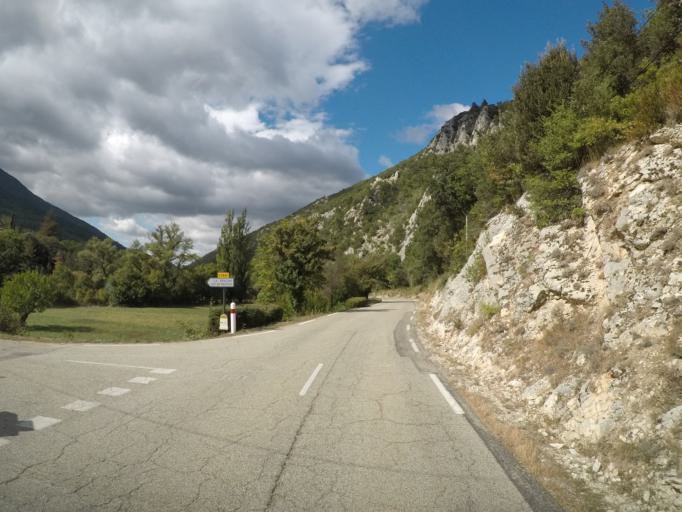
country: FR
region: Rhone-Alpes
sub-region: Departement de la Drome
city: Buis-les-Baronnies
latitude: 44.1921
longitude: 5.3310
